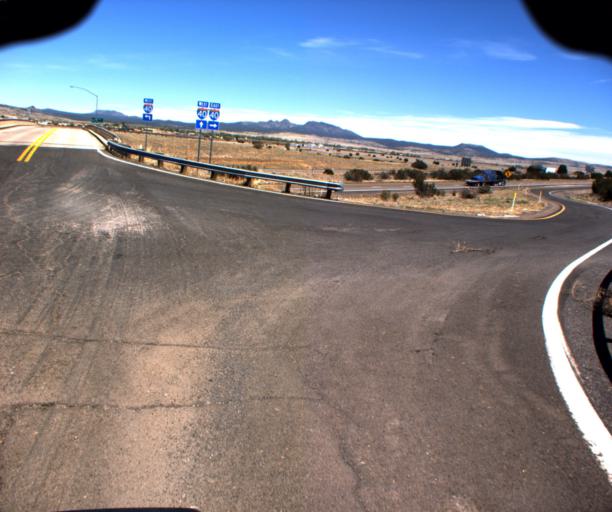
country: US
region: Arizona
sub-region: Mohave County
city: Peach Springs
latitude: 35.3196
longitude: -112.8937
